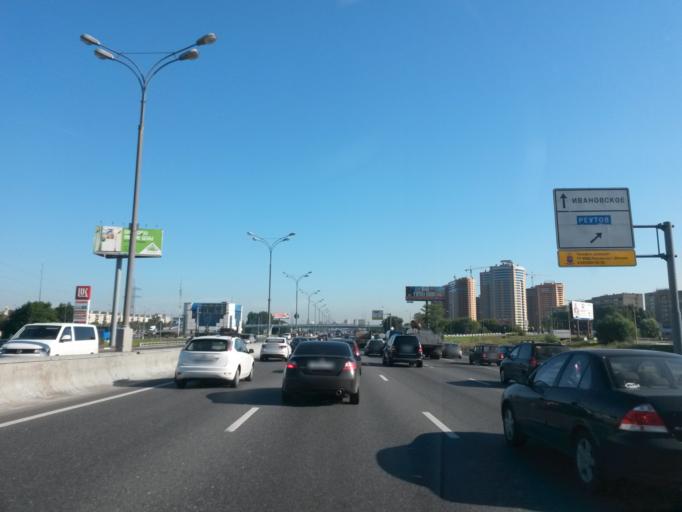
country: RU
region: Moscow
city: Ivanovskoye
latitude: 55.7651
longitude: 37.8431
